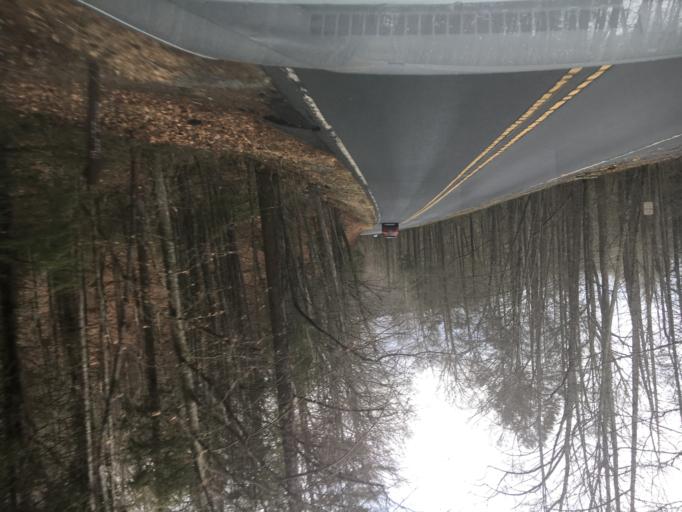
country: US
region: North Carolina
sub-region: Transylvania County
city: Brevard
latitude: 35.2859
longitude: -82.7311
